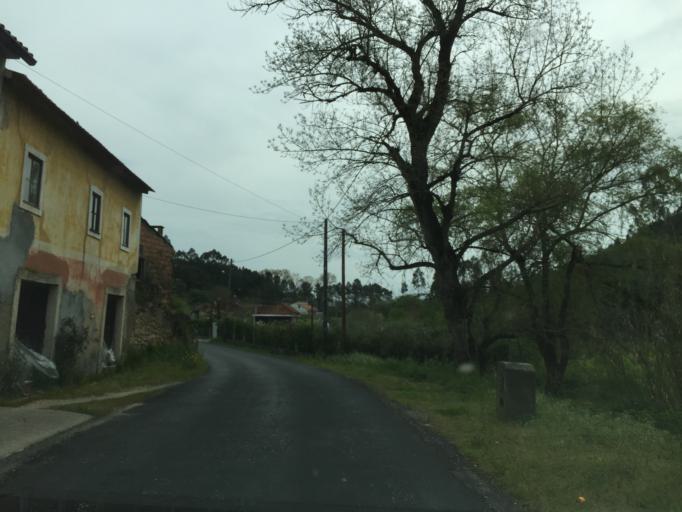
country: PT
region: Leiria
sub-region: Leiria
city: Caranguejeira
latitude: 39.7871
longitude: -8.7321
